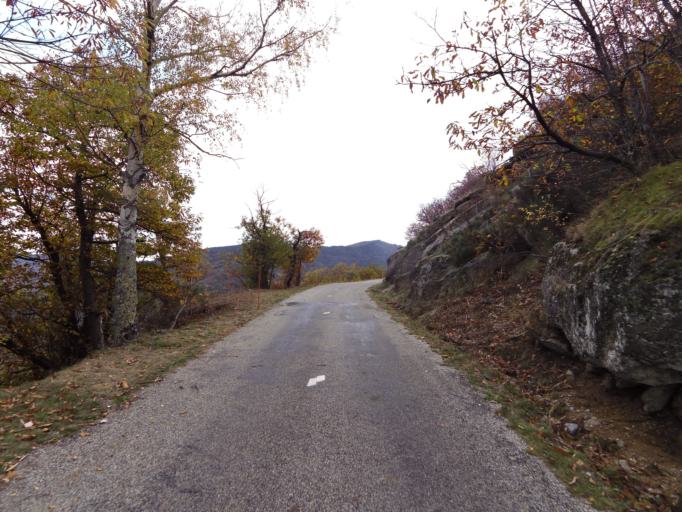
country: FR
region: Rhone-Alpes
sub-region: Departement de l'Ardeche
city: Les Vans
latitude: 44.5255
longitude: 4.0486
